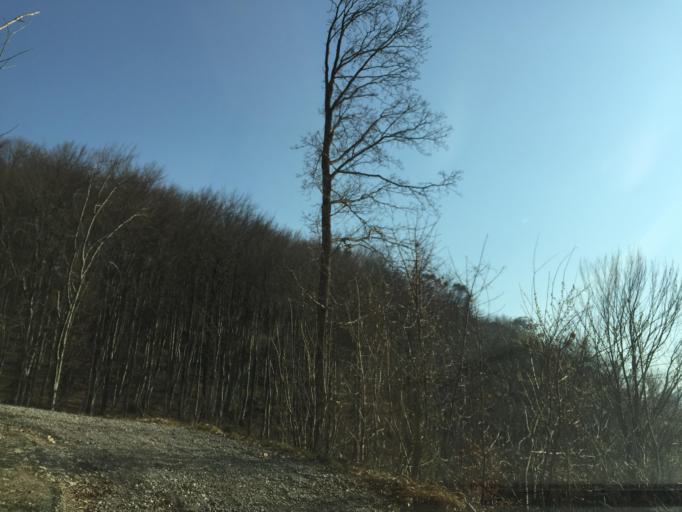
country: IT
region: Friuli Venezia Giulia
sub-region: Provincia di Udine
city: Amaro
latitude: 46.3870
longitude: 13.0680
